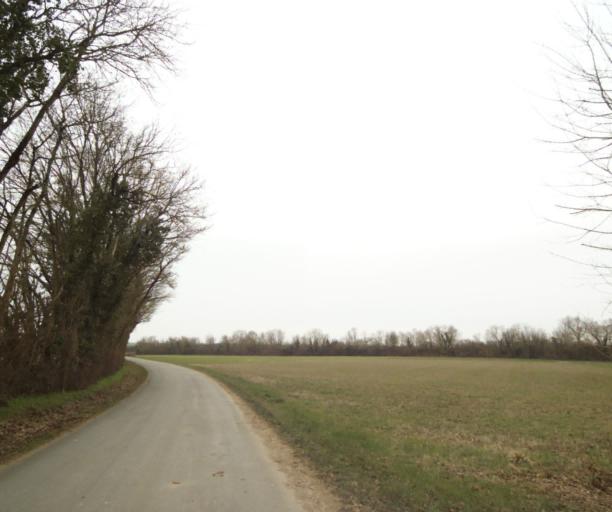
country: FR
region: Poitou-Charentes
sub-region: Departement des Deux-Sevres
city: Magne
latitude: 46.3284
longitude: -0.5281
